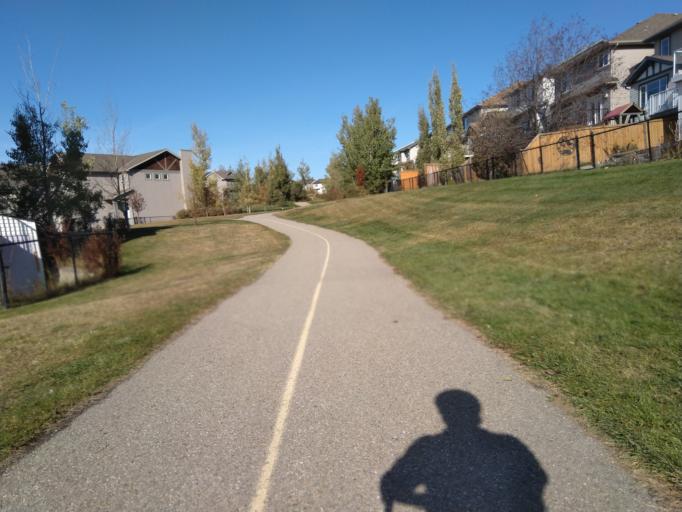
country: CA
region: Alberta
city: Calgary
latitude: 51.1624
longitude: -114.1209
